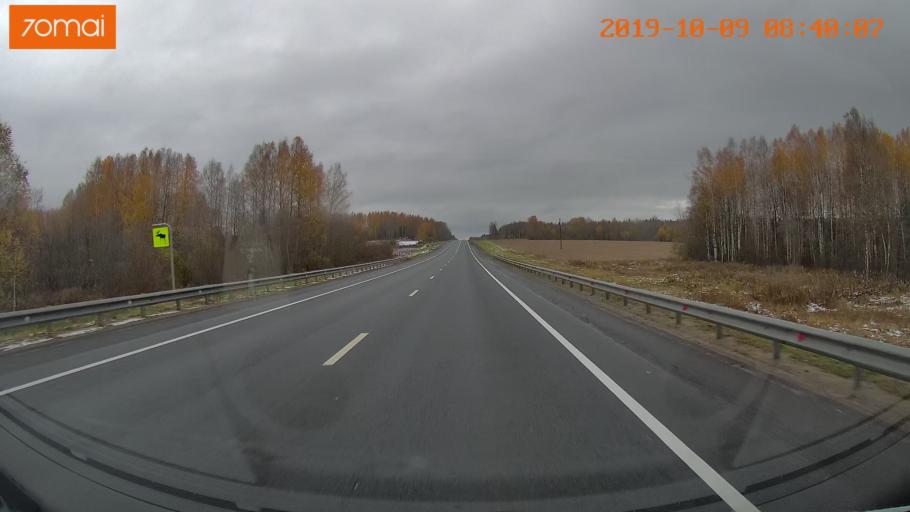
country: RU
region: Vologda
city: Gryazovets
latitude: 58.9816
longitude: 40.1446
